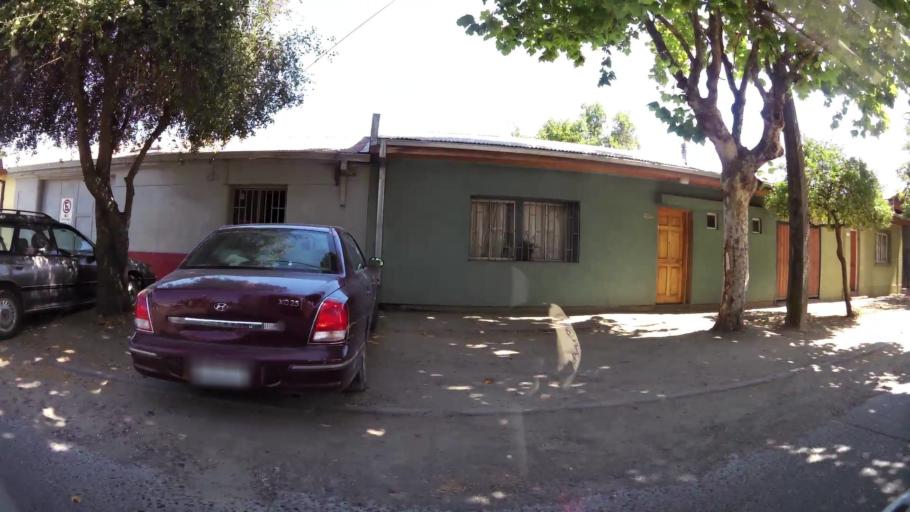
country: CL
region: Maule
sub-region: Provincia de Talca
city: Talca
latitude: -35.4142
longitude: -71.6524
